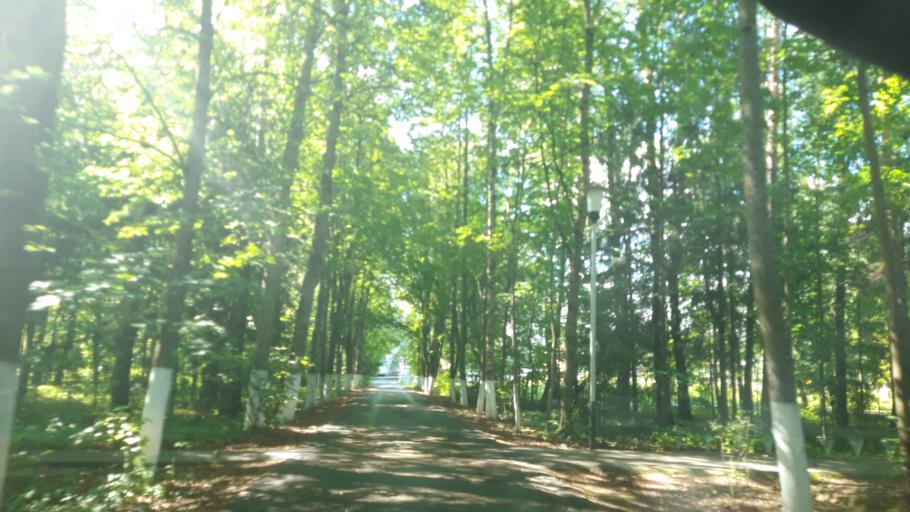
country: RU
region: Moskovskaya
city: Andreyevka
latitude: 55.9846
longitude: 37.1027
